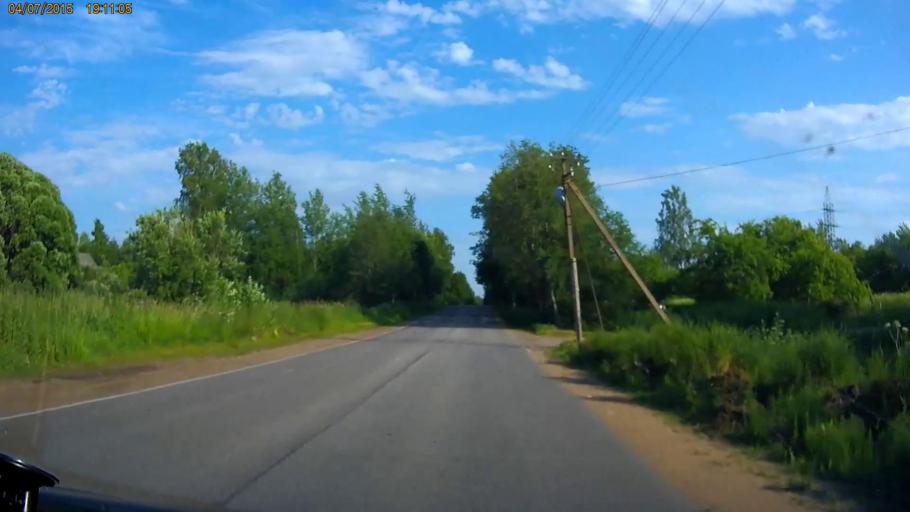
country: RU
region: Leningrad
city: Garbolovo
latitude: 60.3316
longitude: 30.4889
